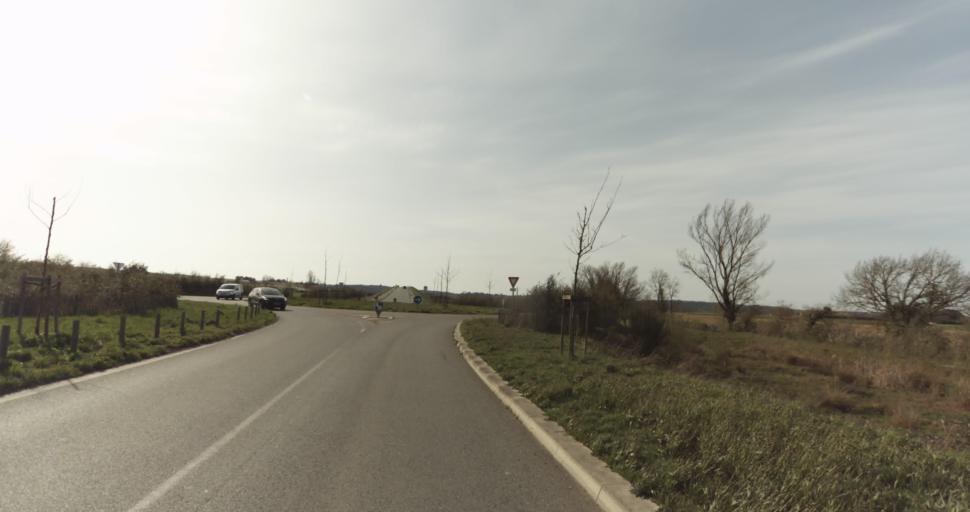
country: FR
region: Midi-Pyrenees
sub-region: Departement de la Haute-Garonne
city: Buzet-sur-Tarn
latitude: 43.7689
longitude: 1.6561
